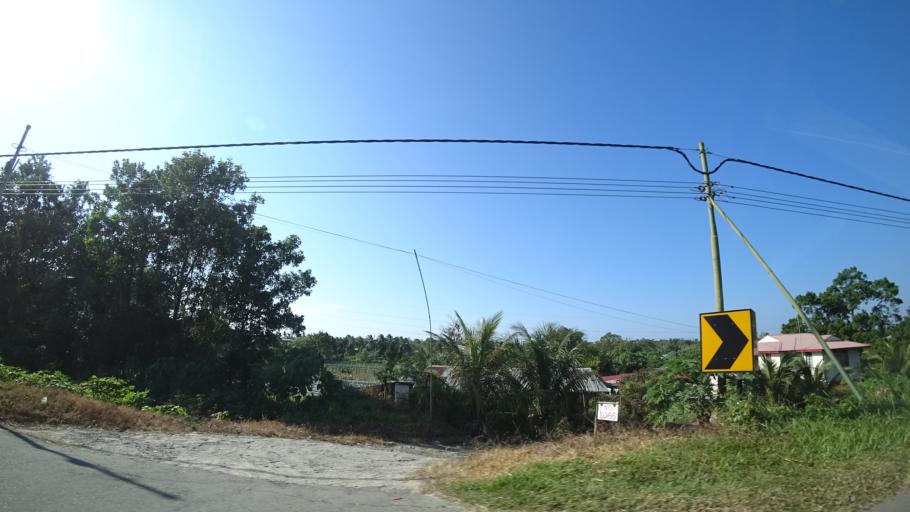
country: BN
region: Tutong
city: Tutong
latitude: 4.6824
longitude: 114.5016
